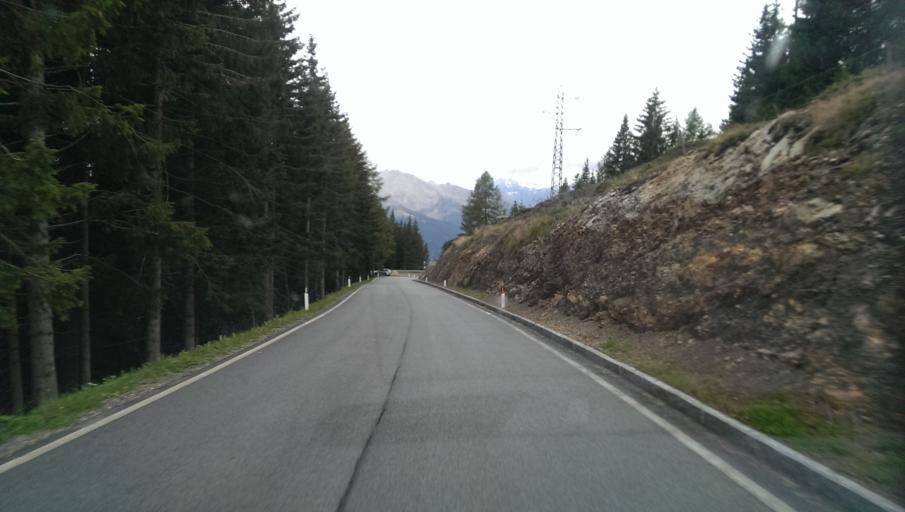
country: IT
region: Trentino-Alto Adige
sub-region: Bolzano
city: Racines
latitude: 46.8343
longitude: 11.3044
